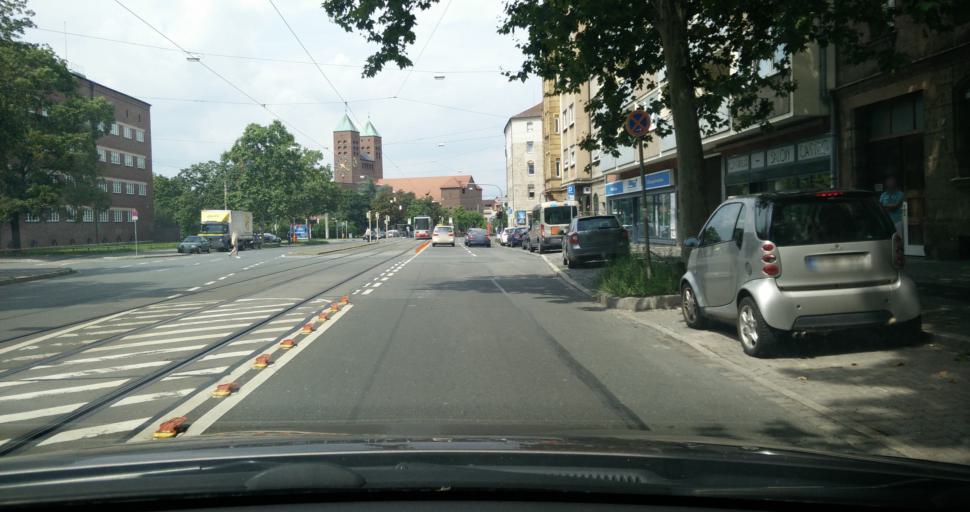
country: DE
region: Bavaria
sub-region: Regierungsbezirk Mittelfranken
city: Nuernberg
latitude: 49.4357
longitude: 11.0927
